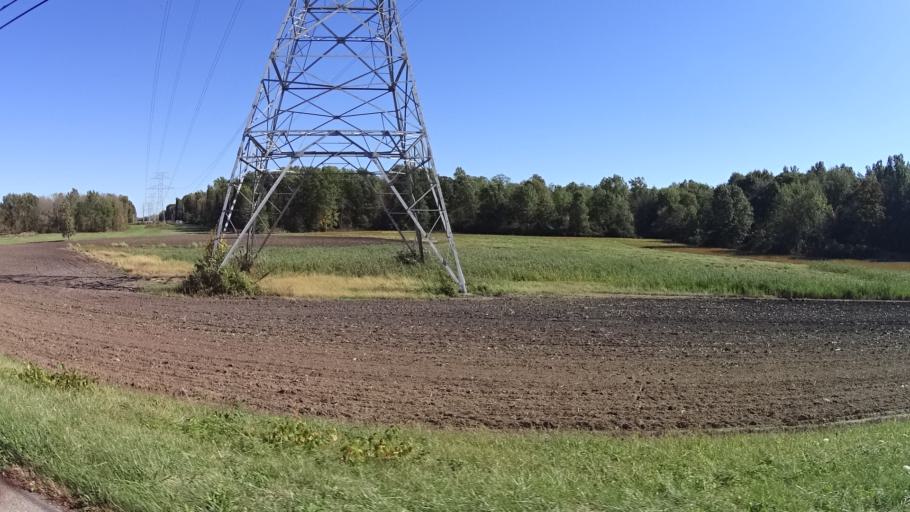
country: US
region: Ohio
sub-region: Lorain County
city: Lorain
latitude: 41.4079
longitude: -82.1702
